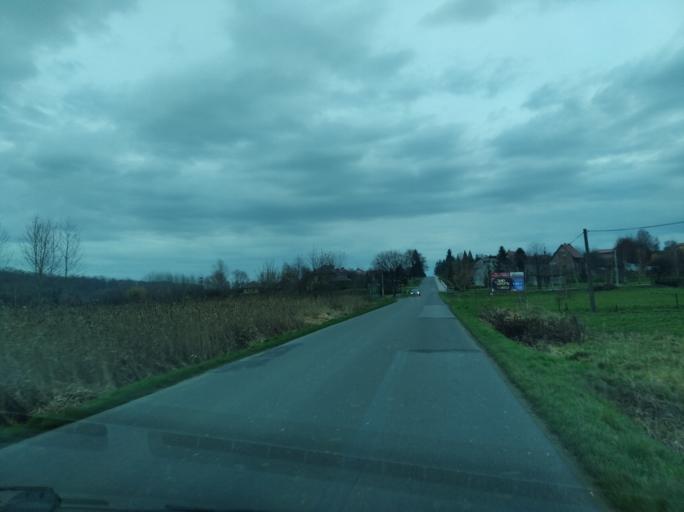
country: PL
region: Subcarpathian Voivodeship
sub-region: Powiat ropczycko-sedziszowski
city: Iwierzyce
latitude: 50.0342
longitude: 21.7482
